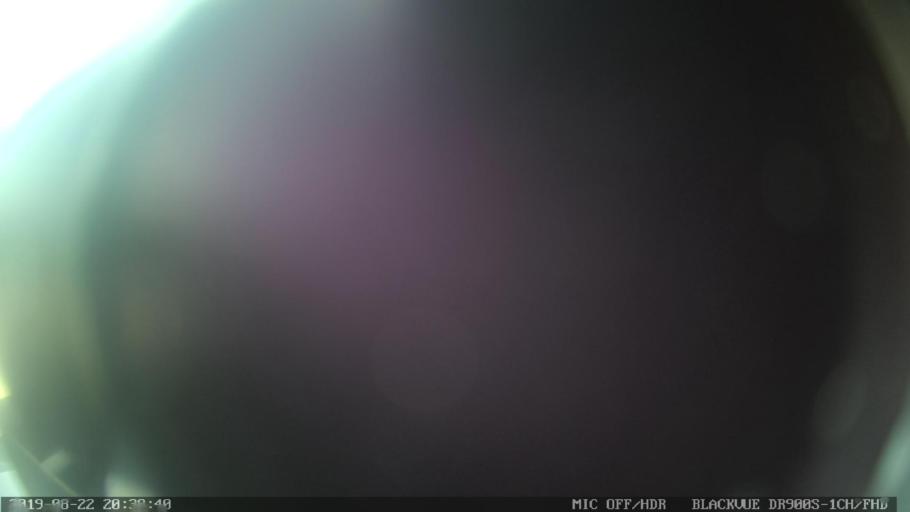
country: PT
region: Castelo Branco
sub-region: Proenca-A-Nova
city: Proenca-a-Nova
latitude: 39.6875
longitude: -7.7525
